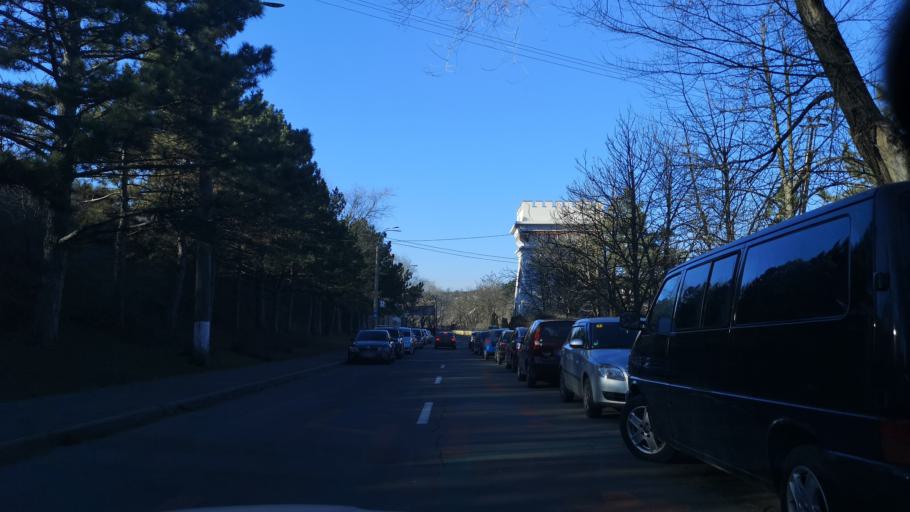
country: MD
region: Chisinau
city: Cricova
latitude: 47.1477
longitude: 28.8617
